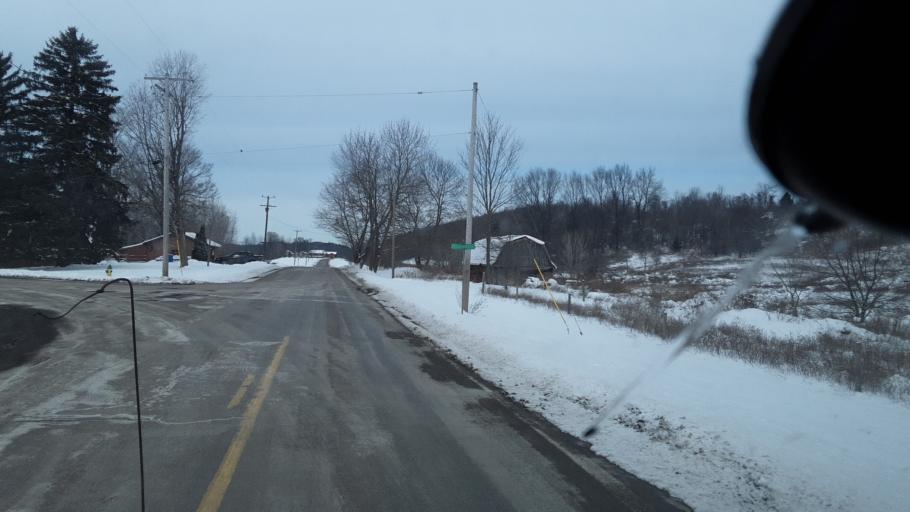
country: US
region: New York
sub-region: Wayne County
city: Lyons
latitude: 43.1045
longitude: -77.0447
